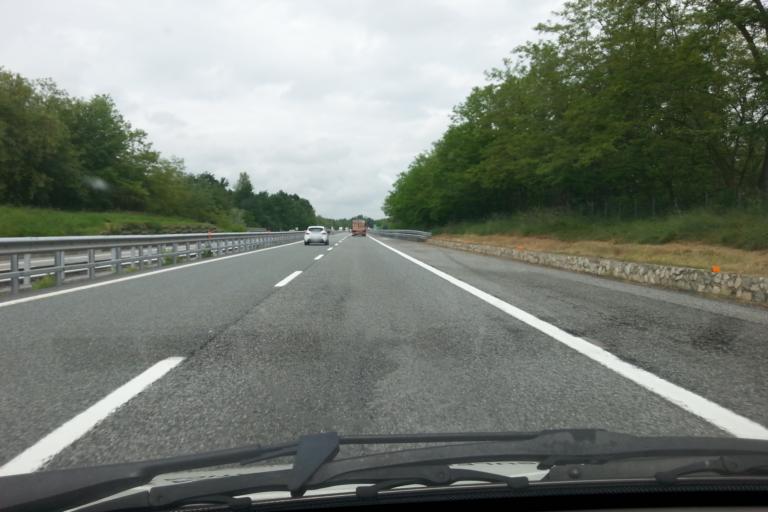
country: IT
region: Piedmont
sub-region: Provincia di Cuneo
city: Lesegno
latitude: 44.3951
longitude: 7.9857
